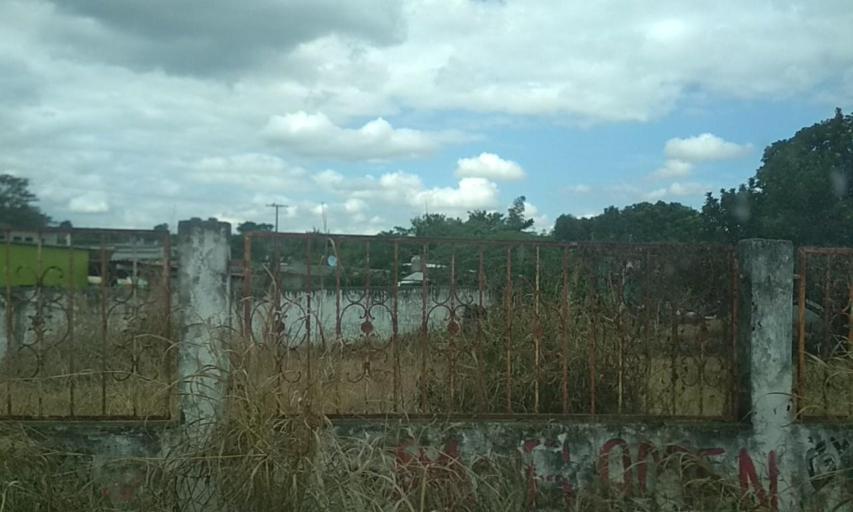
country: MX
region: Veracruz
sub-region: Martinez de la Torre
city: El Progreso
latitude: 20.0948
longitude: -97.0125
